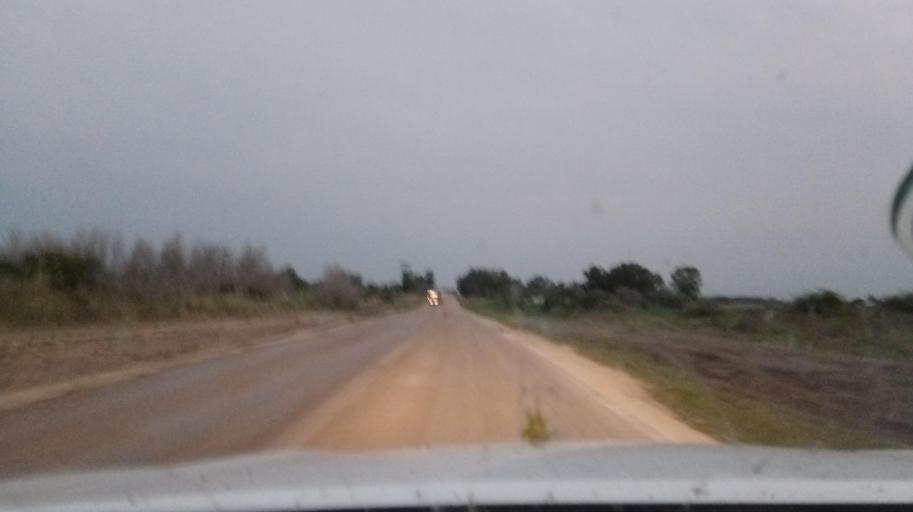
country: UY
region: Canelones
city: Santa Rosa
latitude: -34.5569
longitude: -56.1030
